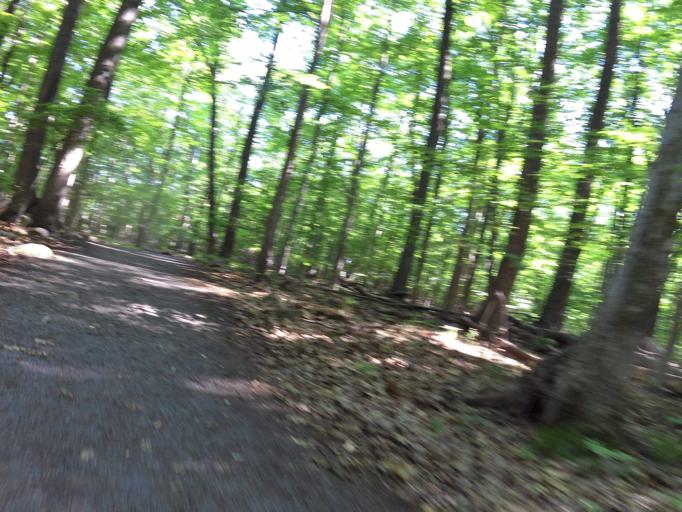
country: CA
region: Ontario
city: Arnprior
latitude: 45.4612
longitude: -76.2679
